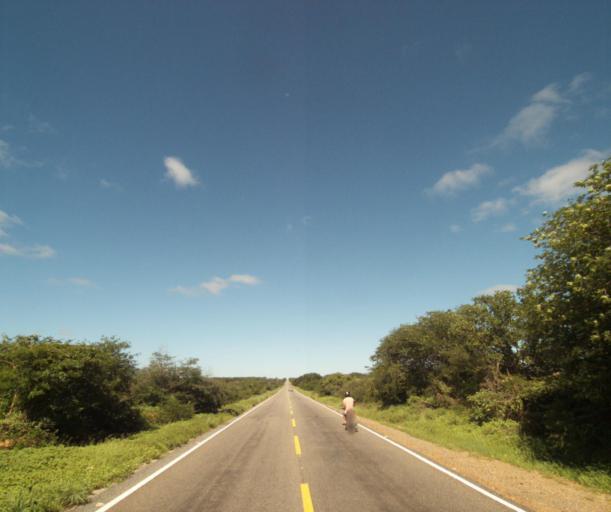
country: BR
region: Bahia
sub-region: Palmas De Monte Alto
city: Palmas de Monte Alto
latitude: -14.2439
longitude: -43.0932
